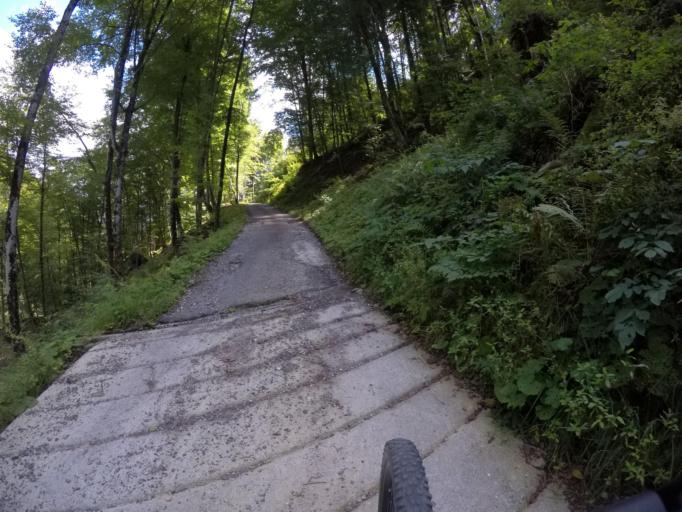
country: IT
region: Friuli Venezia Giulia
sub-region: Provincia di Udine
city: Arta Terme
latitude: 46.4844
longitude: 13.0633
